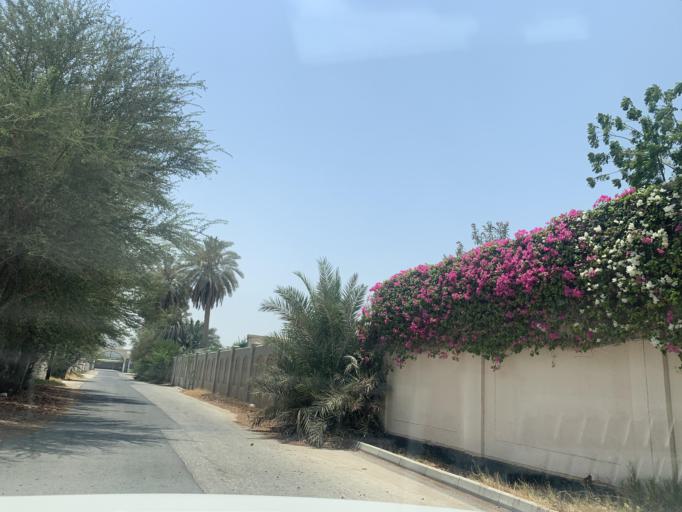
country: BH
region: Manama
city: Jidd Hafs
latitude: 26.2057
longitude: 50.4752
